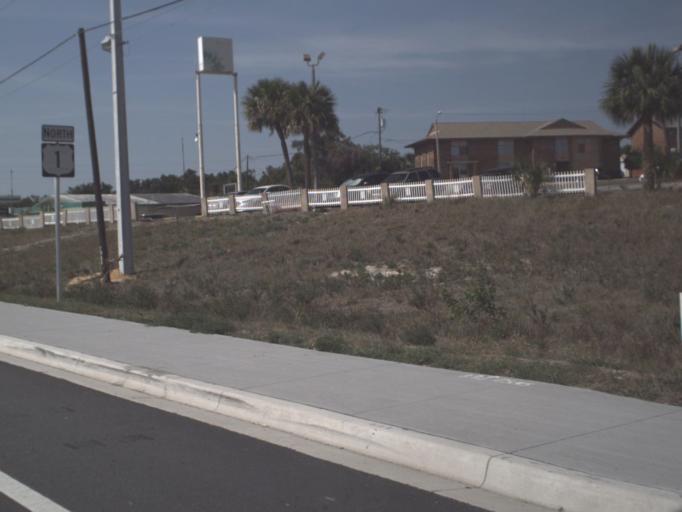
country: US
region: Florida
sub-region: Brevard County
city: Cocoa
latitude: 28.4019
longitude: -80.7536
